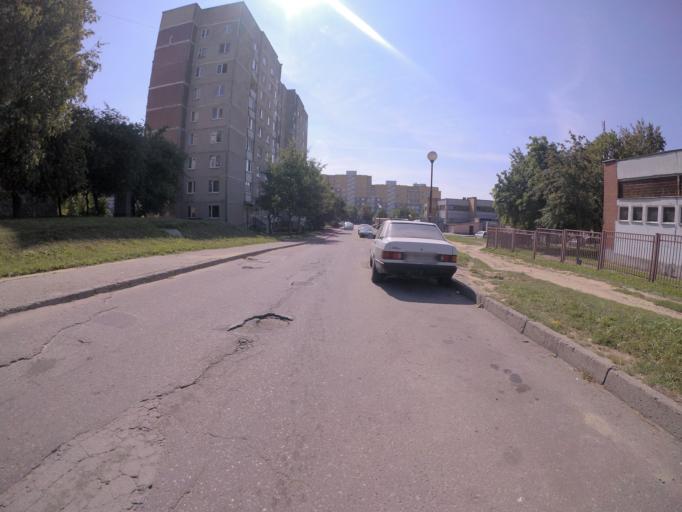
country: BY
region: Grodnenskaya
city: Hrodna
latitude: 53.7024
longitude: 23.8459
